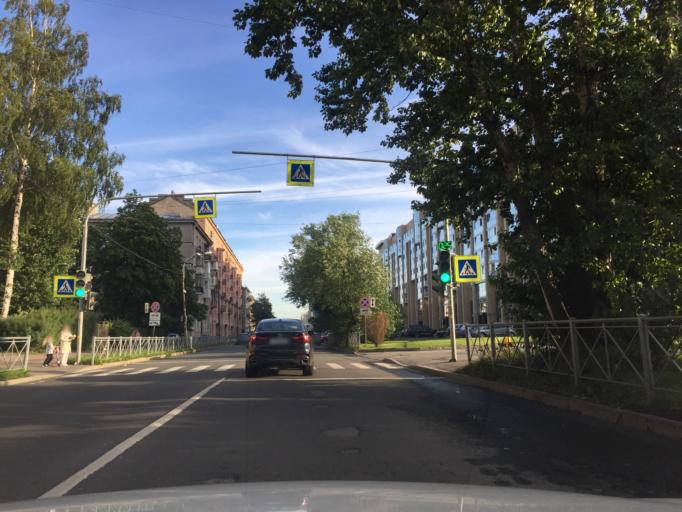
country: RU
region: St.-Petersburg
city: Admiralteisky
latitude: 59.8782
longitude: 30.3133
